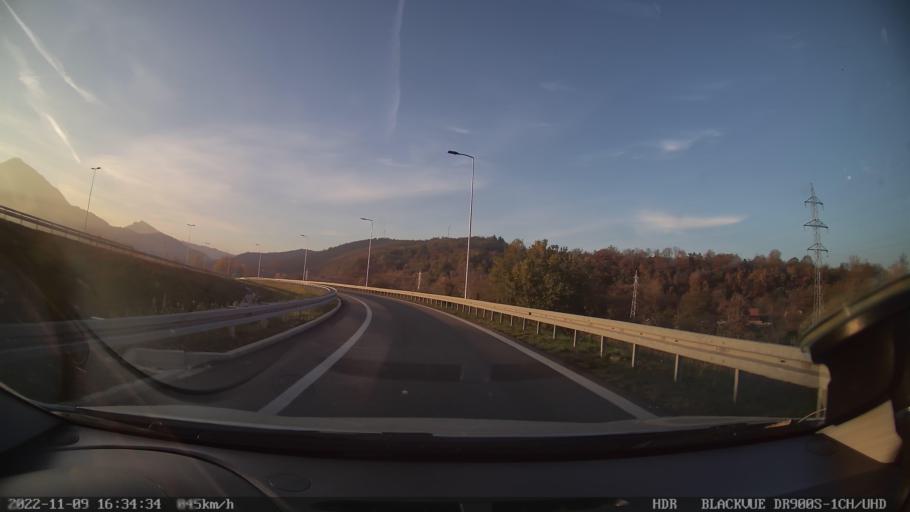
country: RS
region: Central Serbia
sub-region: Moravicki Okrug
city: Cacak
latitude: 43.9022
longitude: 20.2657
